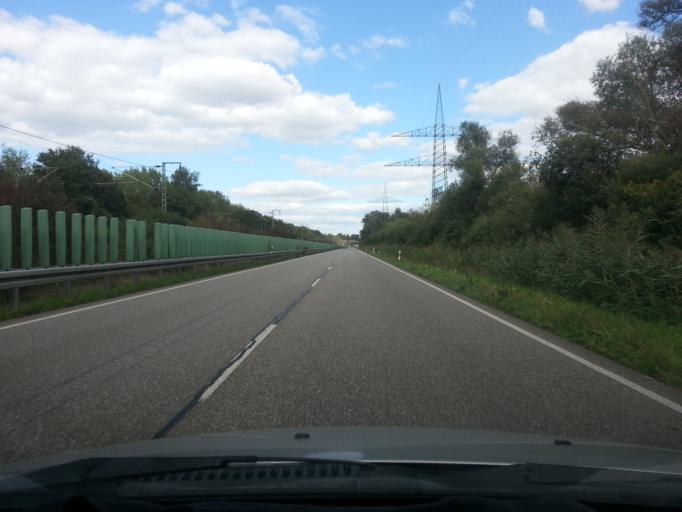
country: DE
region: Baden-Wuerttemberg
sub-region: Karlsruhe Region
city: Waghausel
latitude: 49.2650
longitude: 8.5097
